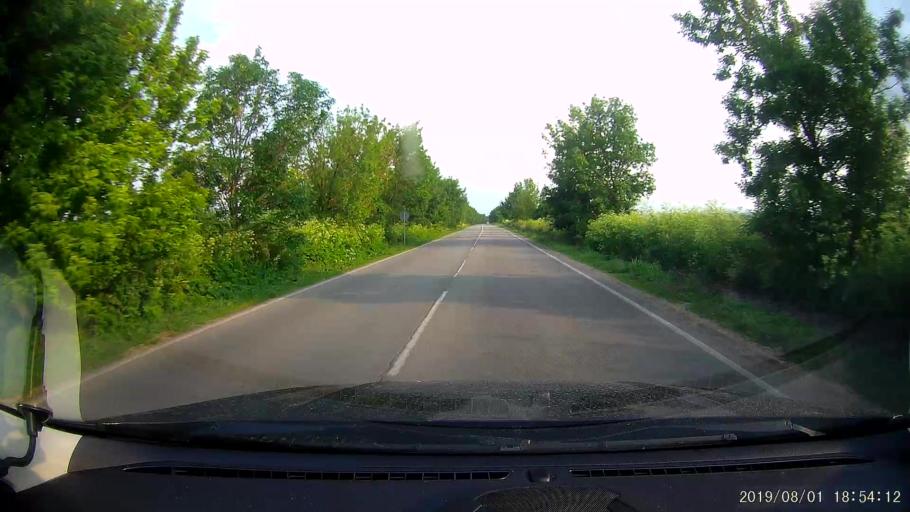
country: BG
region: Shumen
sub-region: Obshtina Shumen
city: Shumen
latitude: 43.2044
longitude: 27.0002
